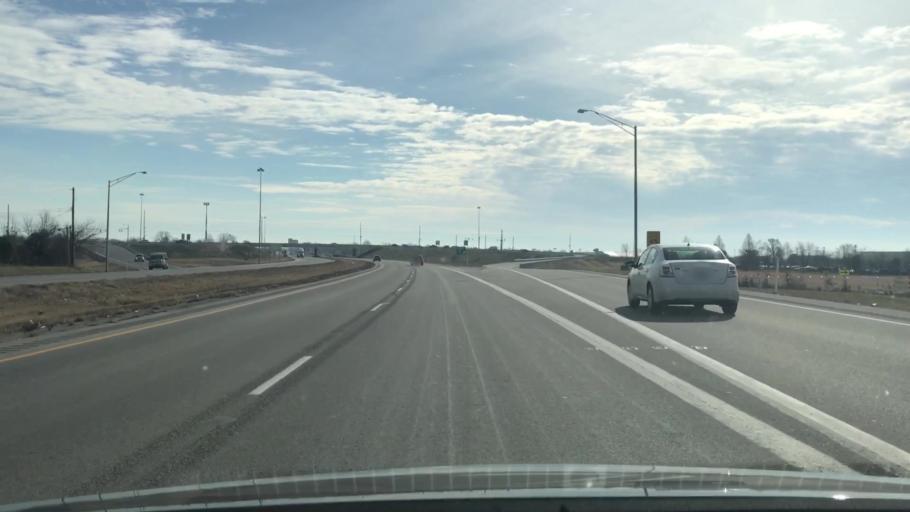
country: US
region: Kentucky
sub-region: Daviess County
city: Owensboro
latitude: 37.7460
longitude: -87.1538
